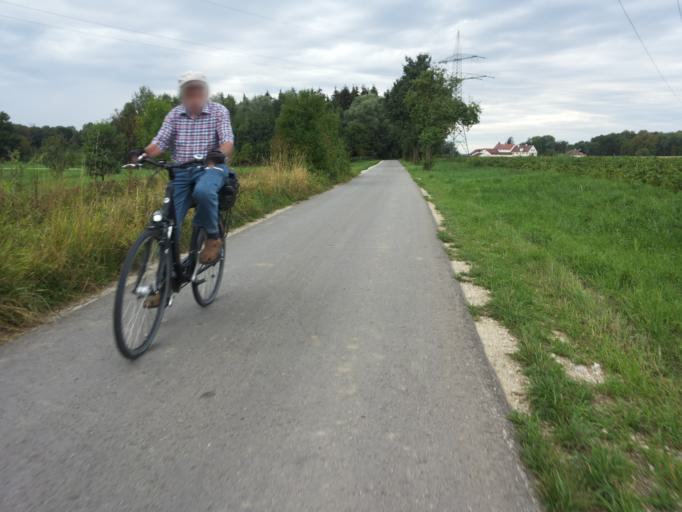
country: DE
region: Bavaria
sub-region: Upper Bavaria
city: Gaimersheim
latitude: 48.7676
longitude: 11.3620
